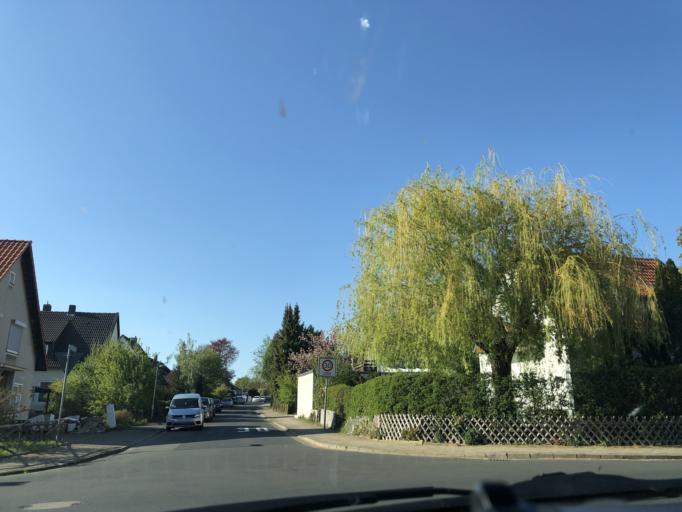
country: DE
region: Lower Saxony
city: Wolfenbuettel
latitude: 52.1705
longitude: 10.5616
